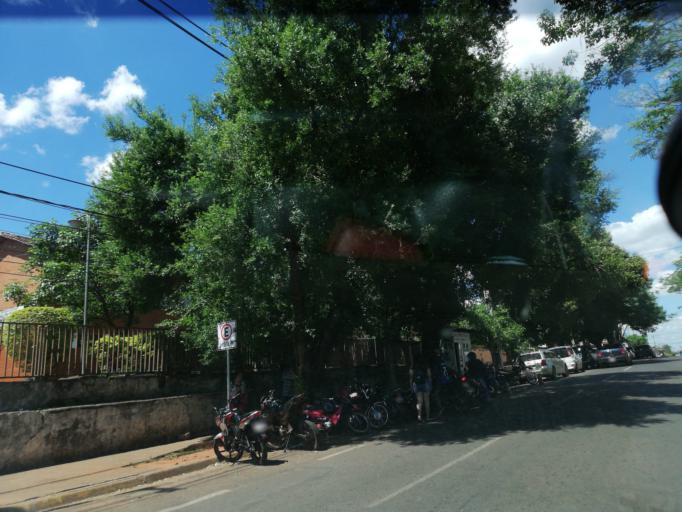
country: PY
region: Itapua
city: Encarnacion
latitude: -27.3397
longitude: -55.8657
